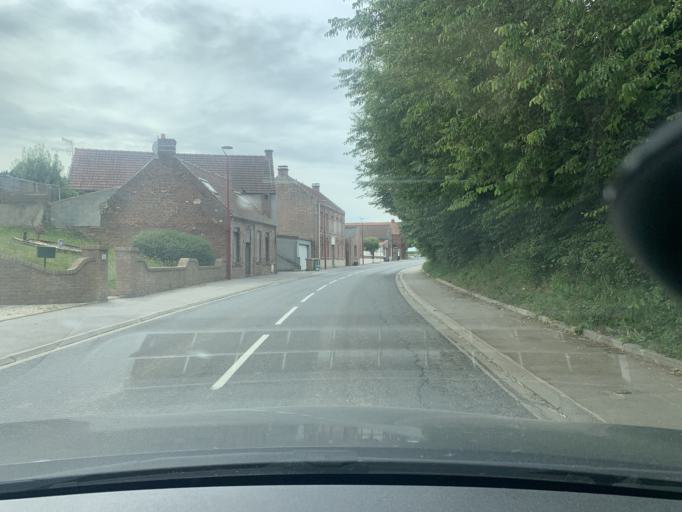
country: FR
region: Nord-Pas-de-Calais
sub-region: Departement du Nord
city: Marcoing
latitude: 50.1365
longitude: 3.1822
